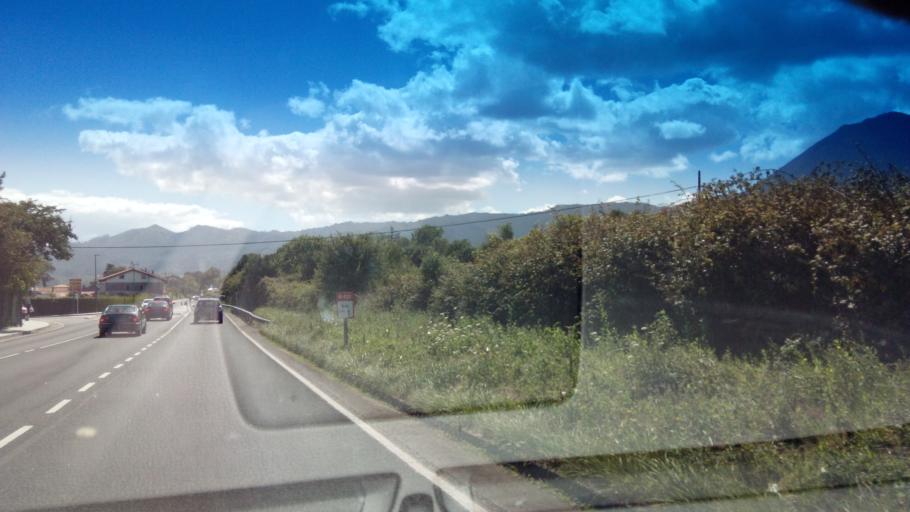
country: ES
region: Asturias
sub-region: Province of Asturias
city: Colunga
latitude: 43.4804
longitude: -5.2321
